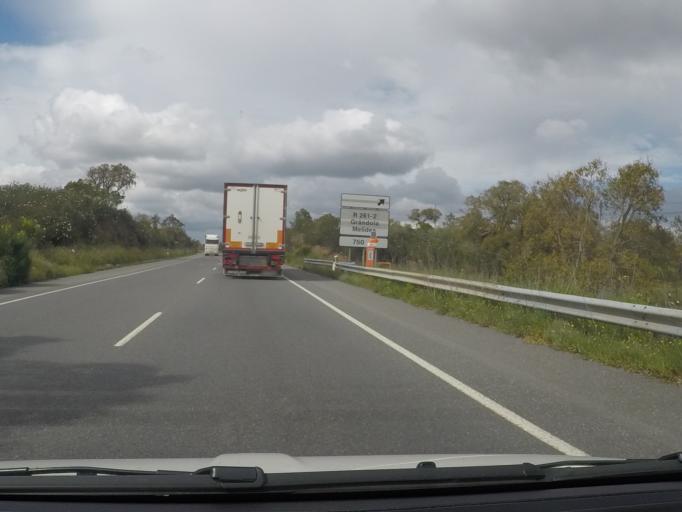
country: PT
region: Setubal
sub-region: Grandola
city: Grandola
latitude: 38.1464
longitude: -8.6502
